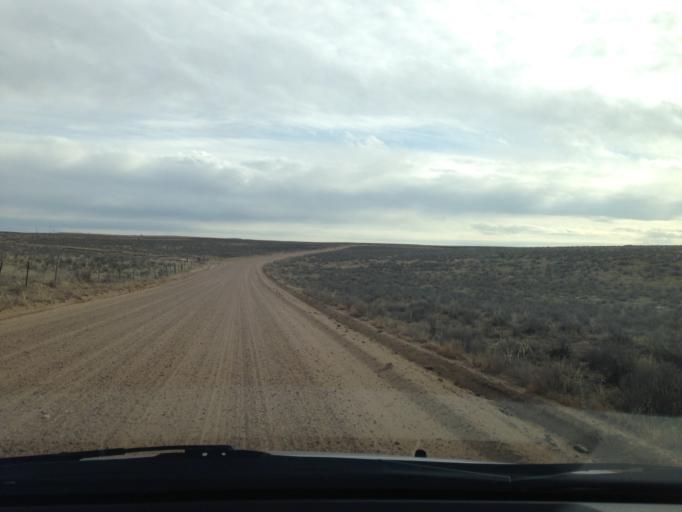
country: US
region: Colorado
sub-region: Weld County
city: Keenesburg
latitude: 40.2777
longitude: -104.2068
